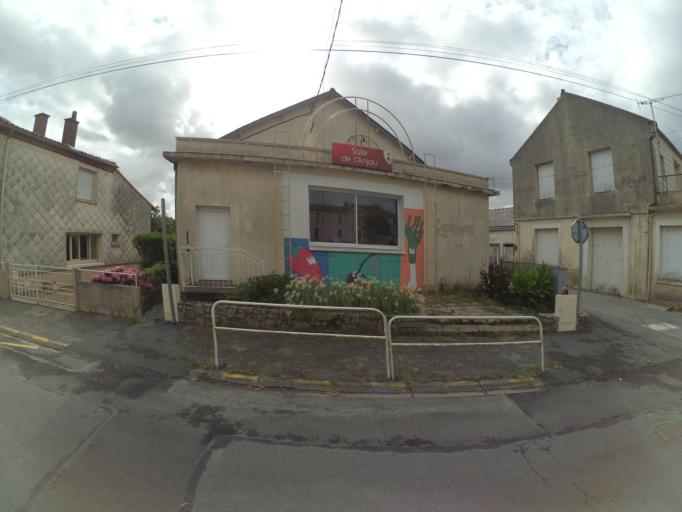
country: FR
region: Pays de la Loire
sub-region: Departement de Maine-et-Loire
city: Villedieu-la-Blouere
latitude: 47.1494
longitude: -1.0613
